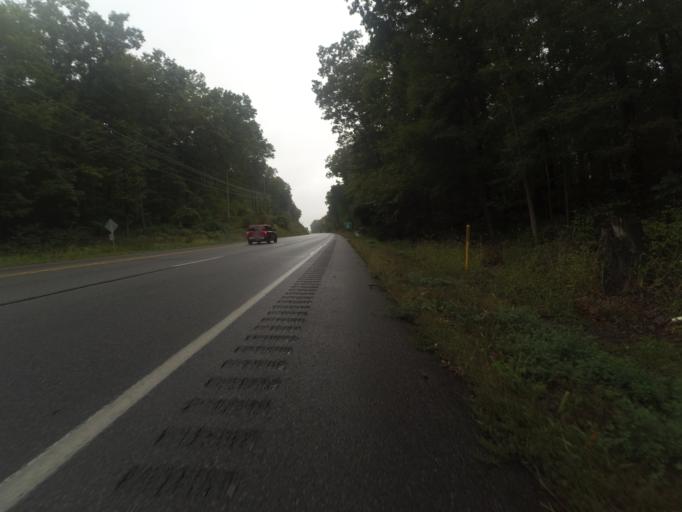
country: US
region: Pennsylvania
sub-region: Huntingdon County
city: Huntingdon
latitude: 40.4970
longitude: -78.0525
